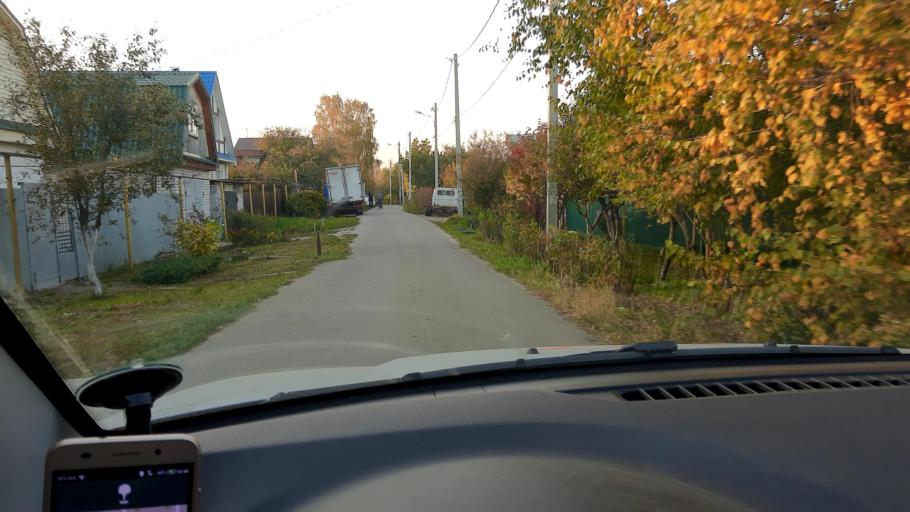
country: RU
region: Nizjnij Novgorod
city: Nizhniy Novgorod
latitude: 56.2793
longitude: 43.8875
